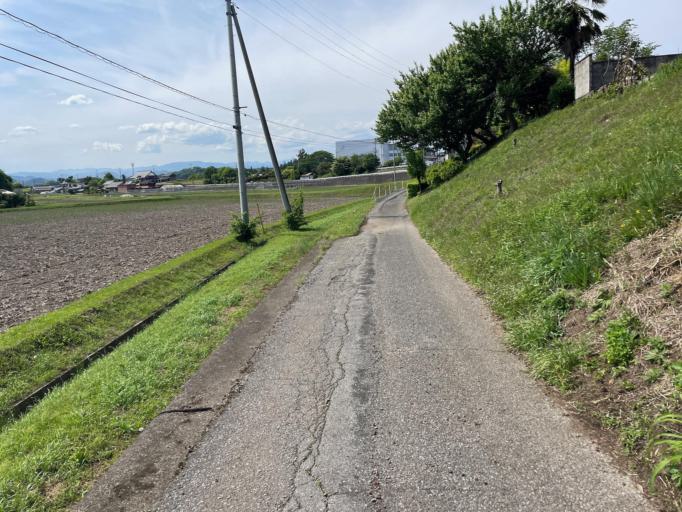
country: JP
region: Tochigi
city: Kanuma
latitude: 36.4846
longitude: 139.7607
